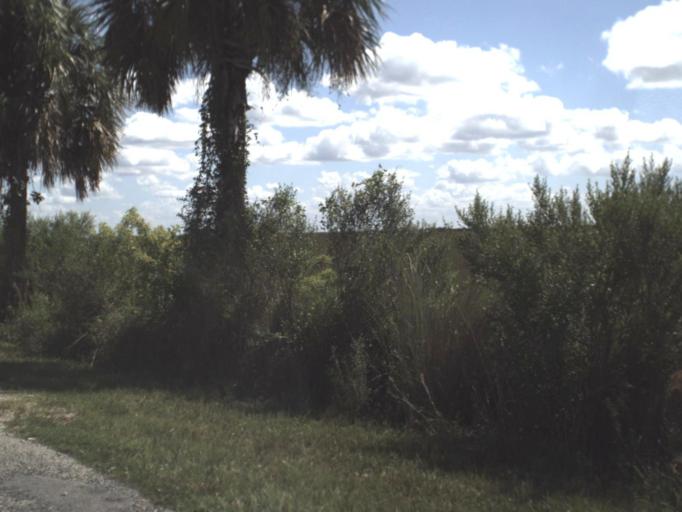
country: US
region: Florida
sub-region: Collier County
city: Marco
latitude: 25.9252
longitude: -81.4235
